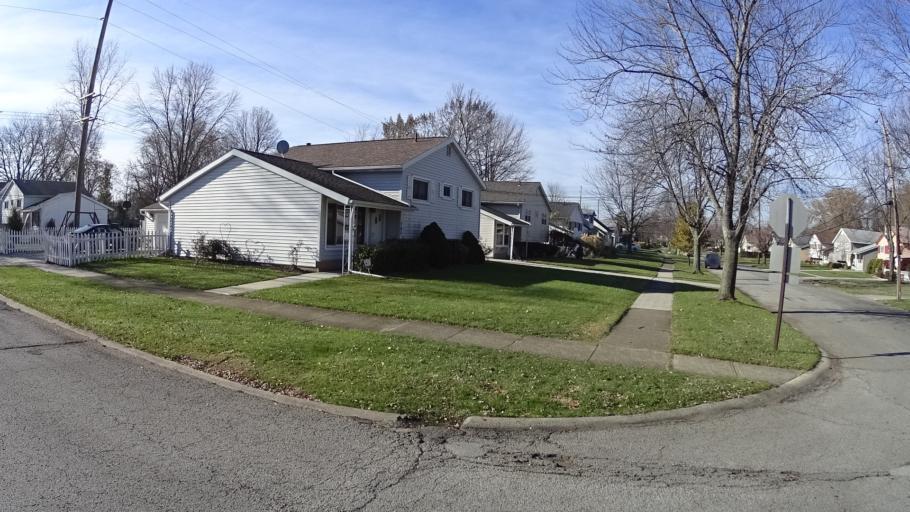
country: US
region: Ohio
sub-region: Lorain County
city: Sheffield
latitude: 41.4032
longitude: -82.0745
